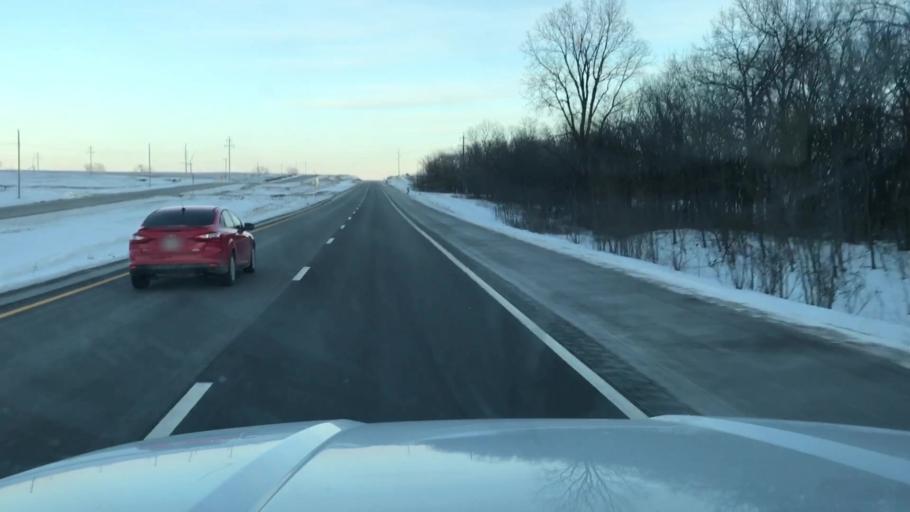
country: US
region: Missouri
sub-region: DeKalb County
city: Maysville
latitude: 39.7619
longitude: -94.4567
